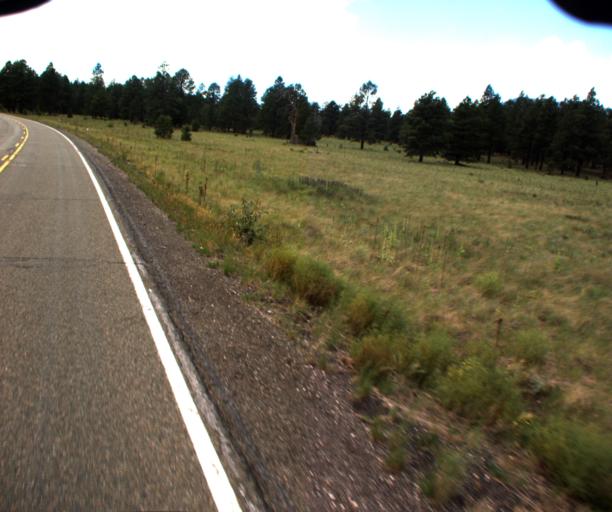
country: US
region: Arizona
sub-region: Coconino County
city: Parks
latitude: 35.3955
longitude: -111.7681
